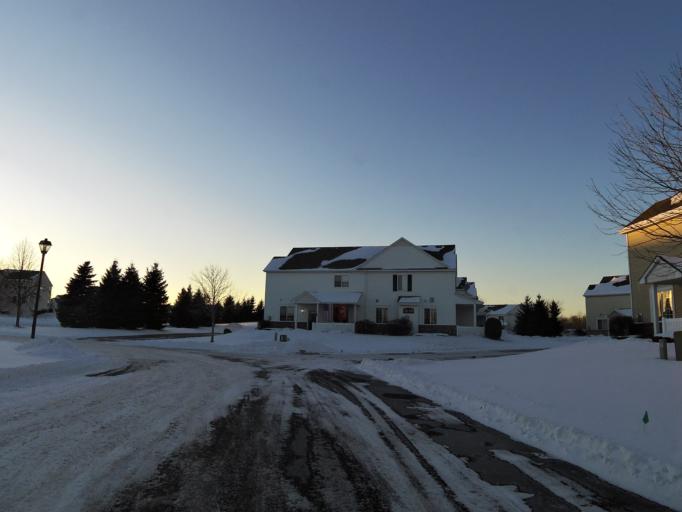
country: US
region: Minnesota
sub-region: Dakota County
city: Rosemount
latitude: 44.7425
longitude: -93.1038
